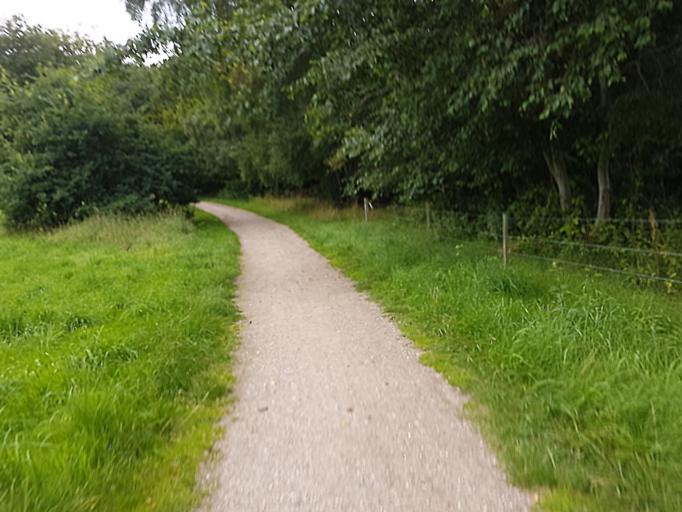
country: DK
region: Capital Region
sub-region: Fureso Kommune
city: Vaerlose
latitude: 55.7937
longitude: 12.3601
